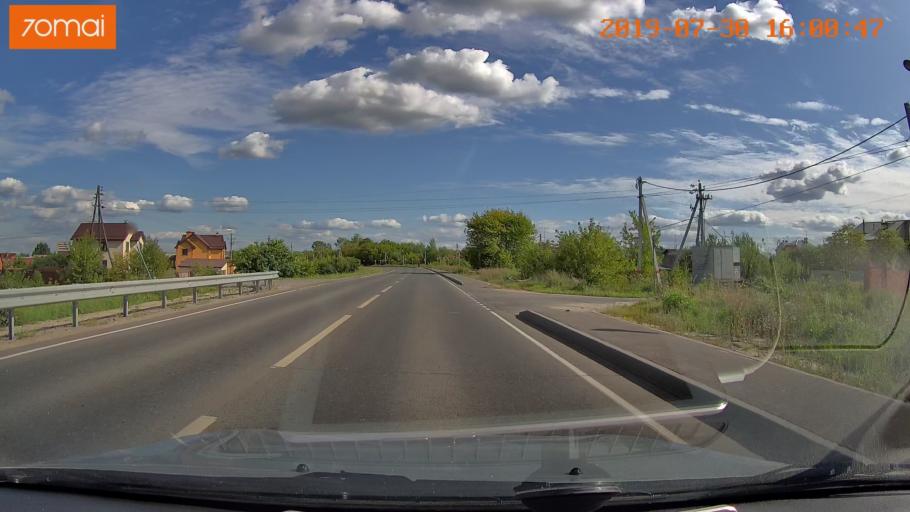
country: RU
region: Moskovskaya
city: Voskresensk
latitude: 55.2965
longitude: 38.6674
